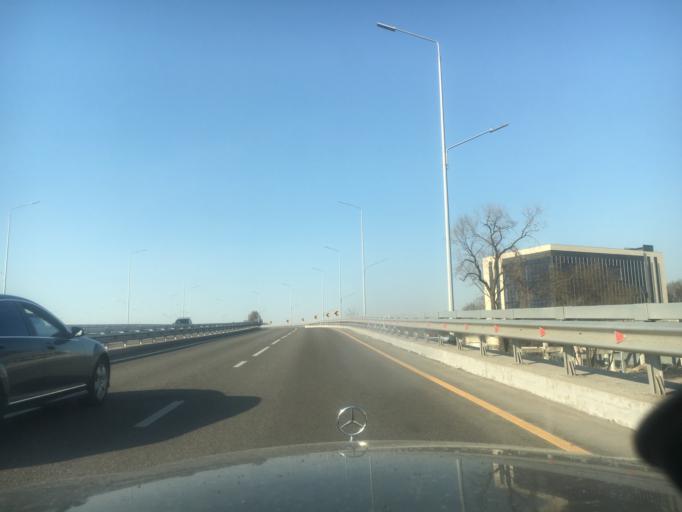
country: KZ
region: Almaty Qalasy
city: Almaty
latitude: 43.2734
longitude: 76.9449
